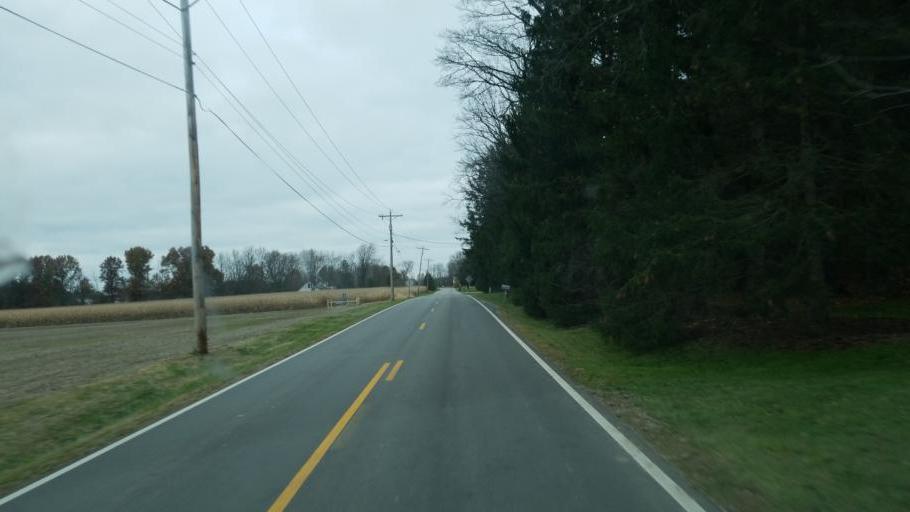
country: US
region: Ohio
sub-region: Franklin County
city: New Albany
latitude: 40.1531
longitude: -82.8392
